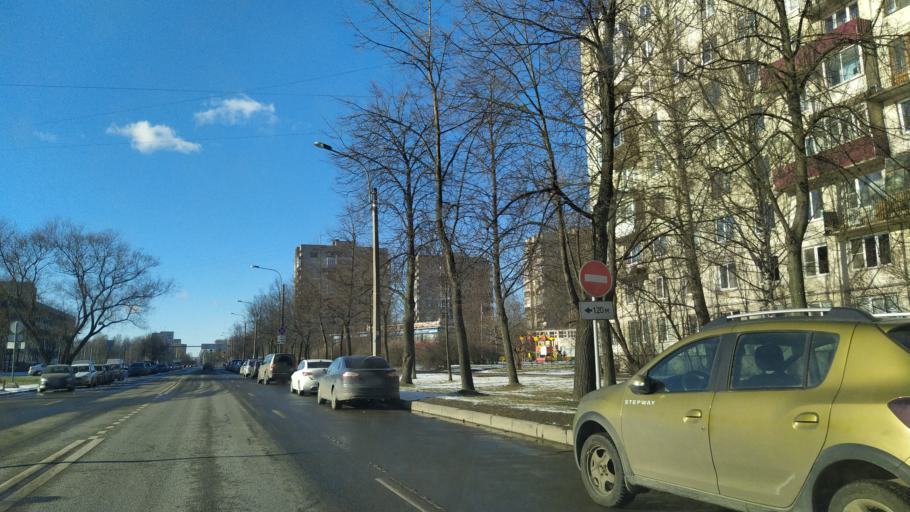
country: RU
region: Leningrad
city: Kalininskiy
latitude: 59.9721
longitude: 30.4197
